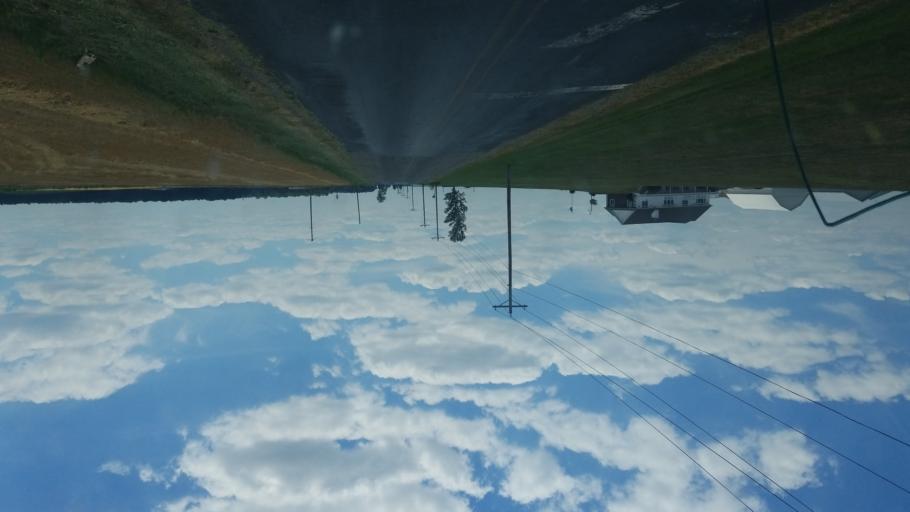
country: US
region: Ohio
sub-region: Williams County
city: Edgerton
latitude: 41.4551
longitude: -84.6912
